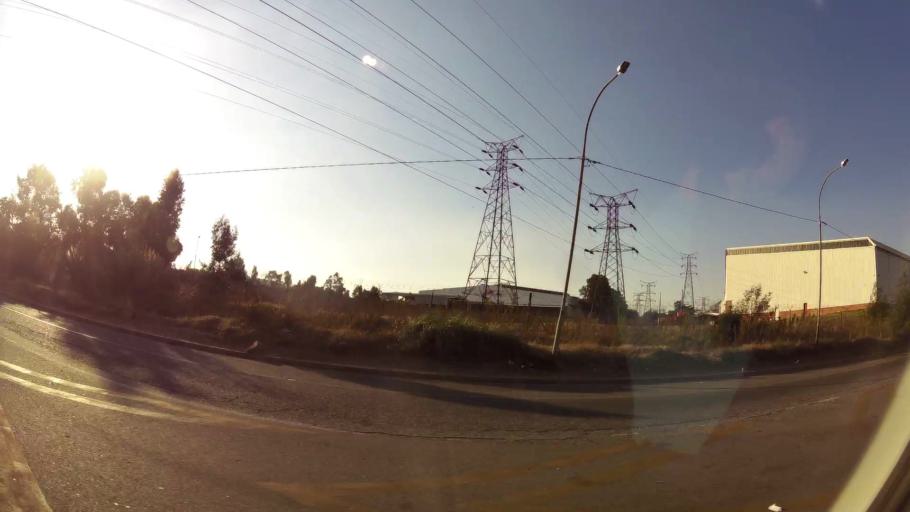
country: ZA
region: Gauteng
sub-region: Ekurhuleni Metropolitan Municipality
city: Germiston
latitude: -26.2103
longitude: 28.1139
